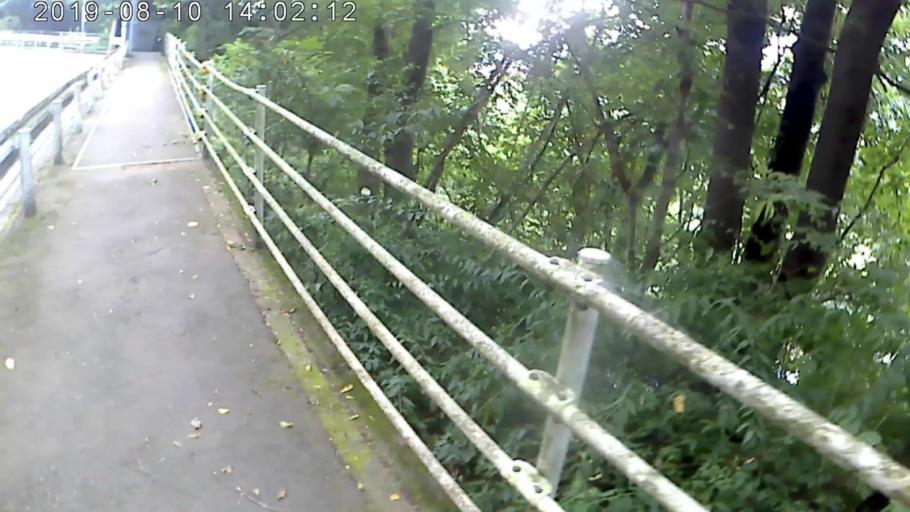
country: JP
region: Yamanashi
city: Uenohara
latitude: 35.6304
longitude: 139.1050
